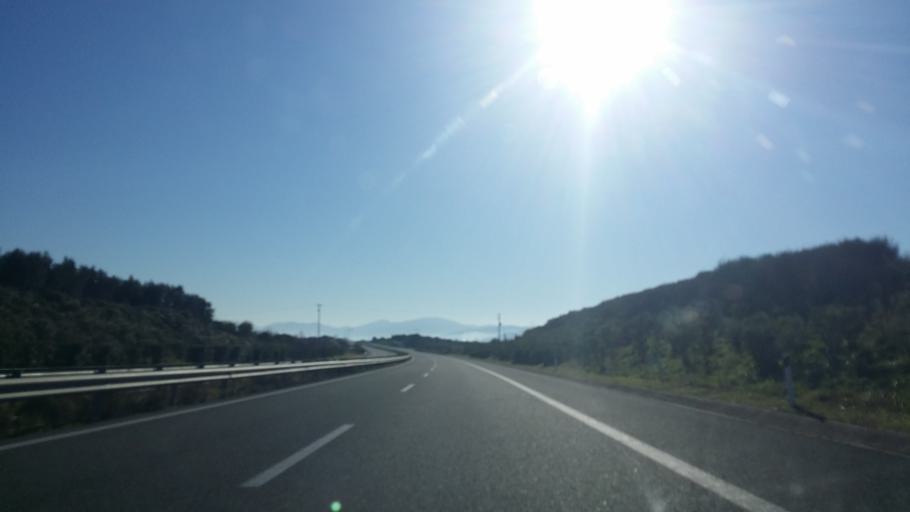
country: GR
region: West Greece
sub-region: Nomos Aitolias kai Akarnanias
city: Fitiai
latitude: 38.6770
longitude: 21.2217
